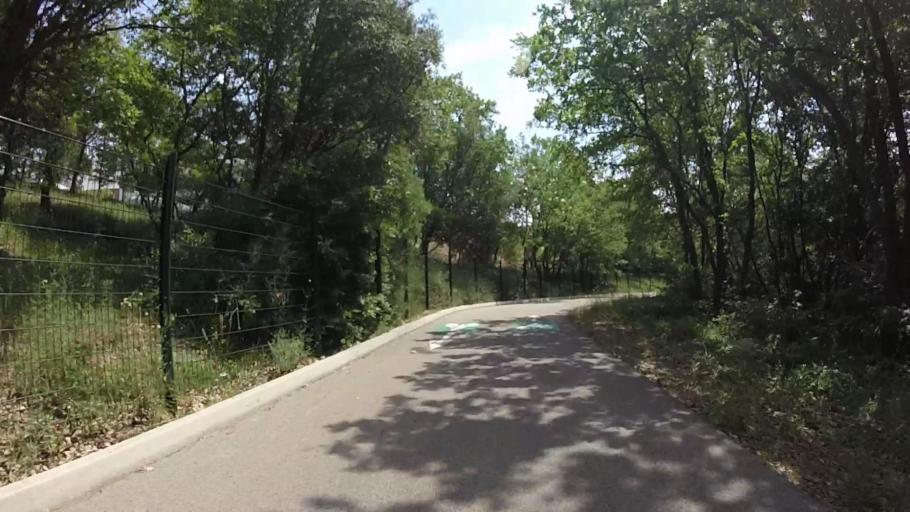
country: FR
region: Provence-Alpes-Cote d'Azur
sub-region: Departement des Alpes-Maritimes
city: Biot
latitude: 43.6251
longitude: 7.0525
